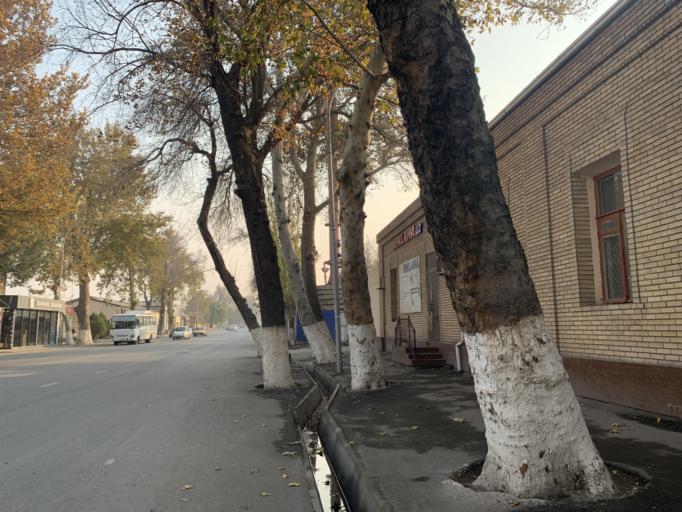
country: UZ
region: Fergana
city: Qo`qon
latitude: 40.5360
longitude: 70.9370
